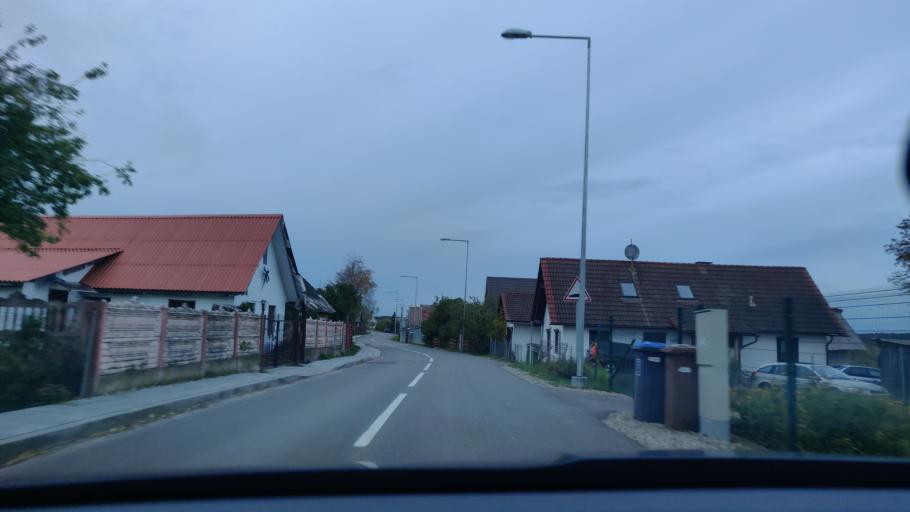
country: LT
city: Lentvaris
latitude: 54.5862
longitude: 25.0513
